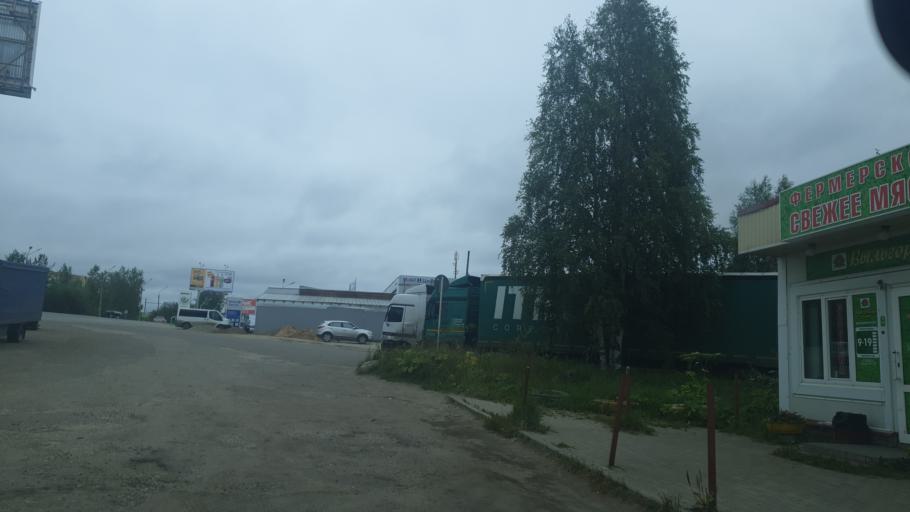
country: RU
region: Komi Republic
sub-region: Syktyvdinskiy Rayon
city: Syktyvkar
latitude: 61.6366
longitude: 50.8134
